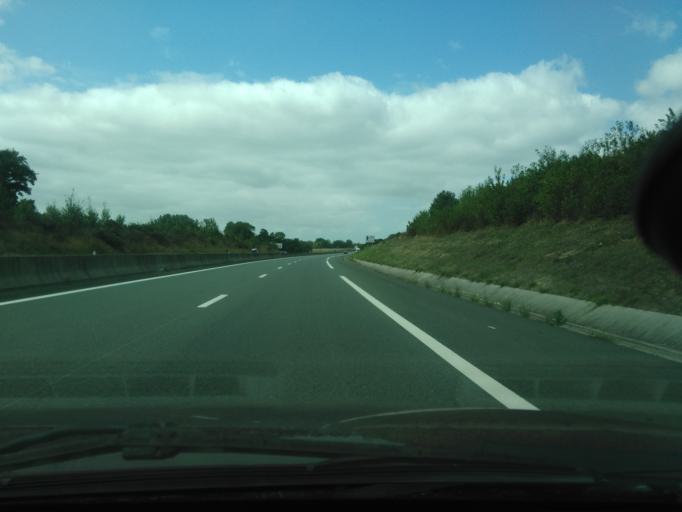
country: FR
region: Pays de la Loire
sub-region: Departement de la Vendee
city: Nesmy
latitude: 46.6299
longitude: -1.4089
